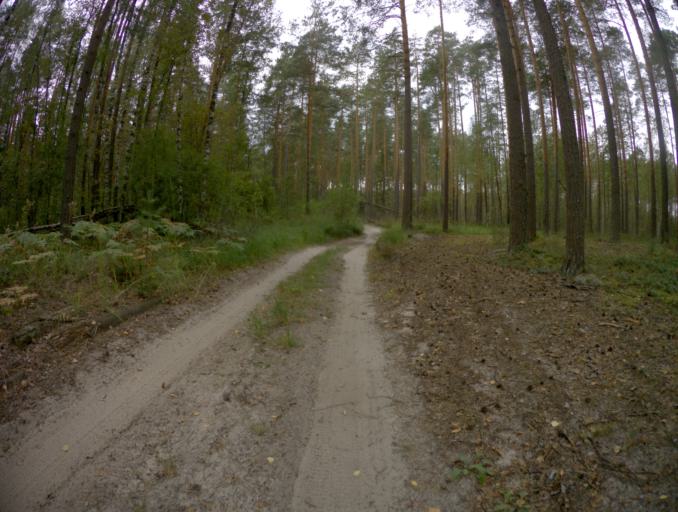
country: RU
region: Vladimir
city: Ivanishchi
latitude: 55.8475
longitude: 40.3463
